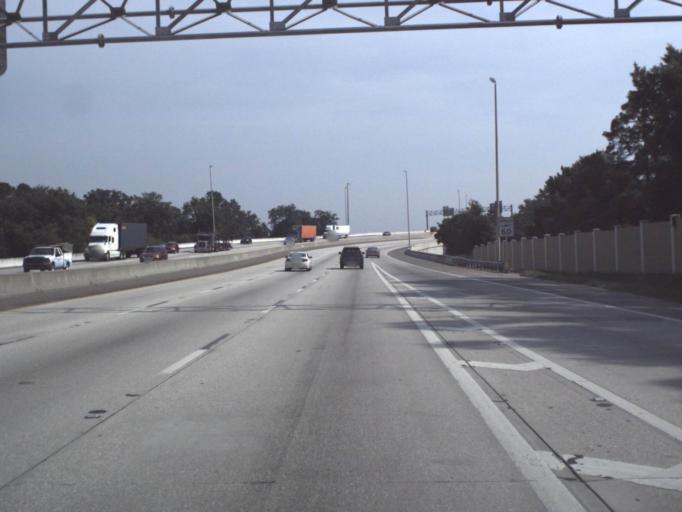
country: US
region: Florida
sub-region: Duval County
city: Jacksonville
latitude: 30.3950
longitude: -81.6679
